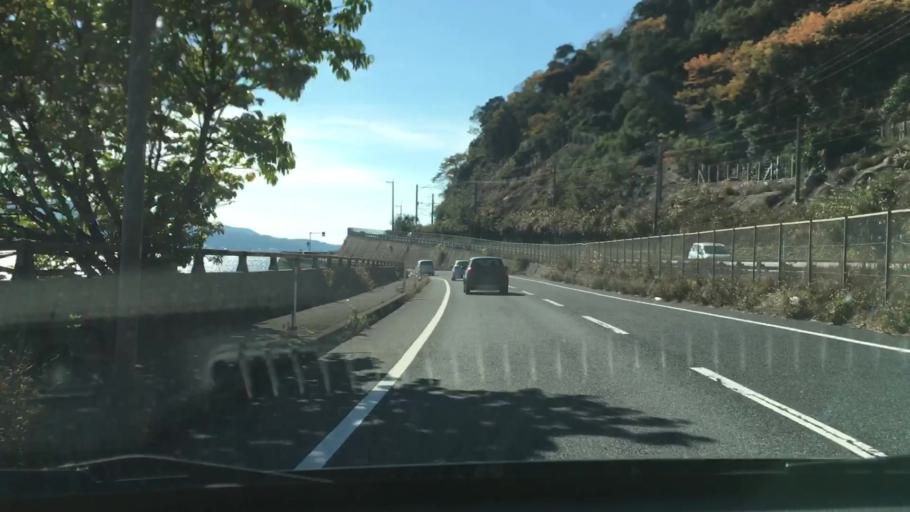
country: JP
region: Kagoshima
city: Kagoshima-shi
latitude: 31.6405
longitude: 130.6024
